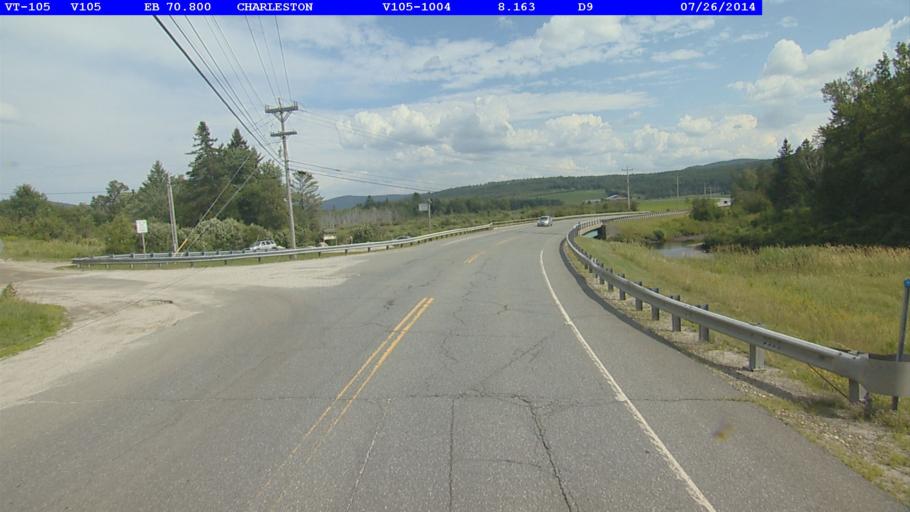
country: US
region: Vermont
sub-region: Orleans County
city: Newport
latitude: 44.8280
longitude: -71.9746
